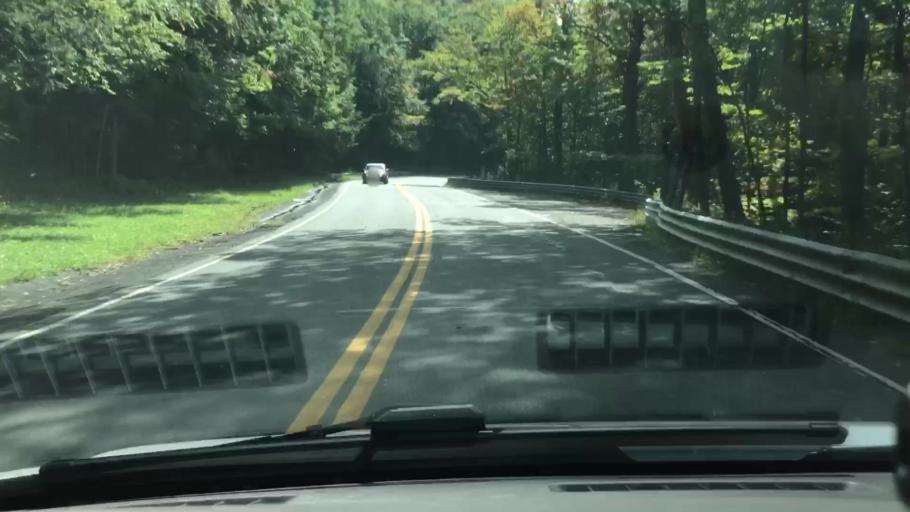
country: US
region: Massachusetts
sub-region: Franklin County
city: Charlemont
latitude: 42.6466
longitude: -72.9921
